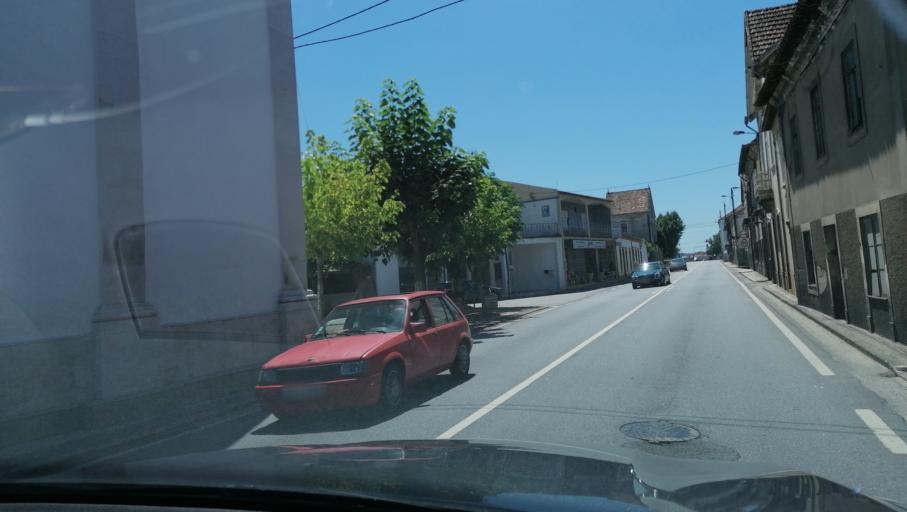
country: PT
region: Aveiro
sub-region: Anadia
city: Sangalhos
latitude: 40.4775
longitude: -8.4539
